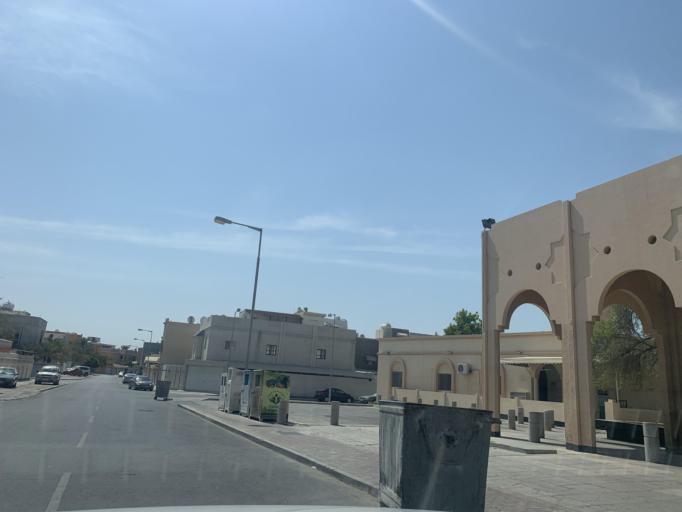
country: BH
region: Central Governorate
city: Madinat Hamad
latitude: 26.1336
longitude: 50.5073
